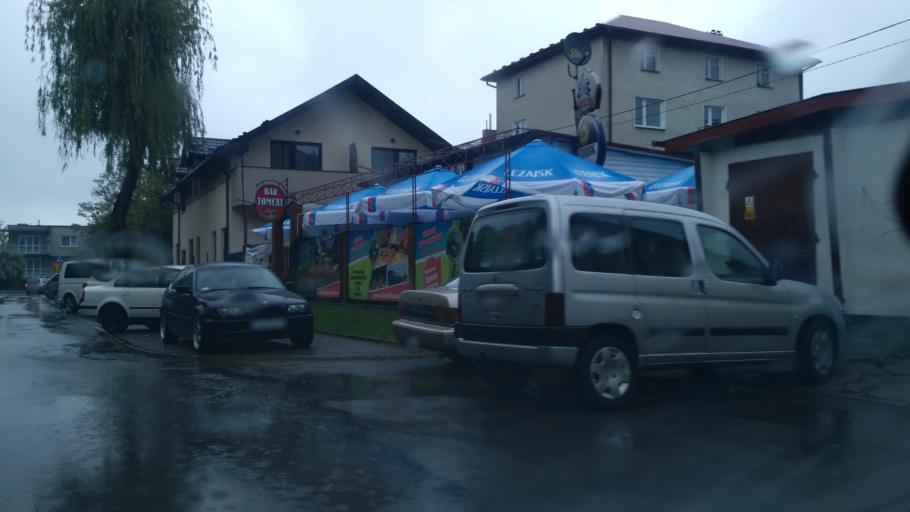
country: PL
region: Subcarpathian Voivodeship
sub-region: Powiat jasielski
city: Jaslo
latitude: 49.7373
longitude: 21.4640
